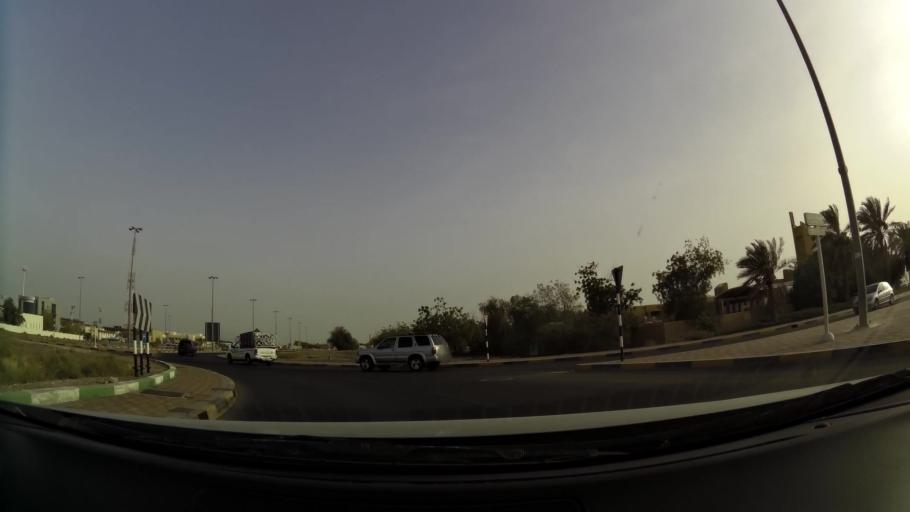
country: AE
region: Abu Dhabi
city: Al Ain
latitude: 24.2370
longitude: 55.7301
